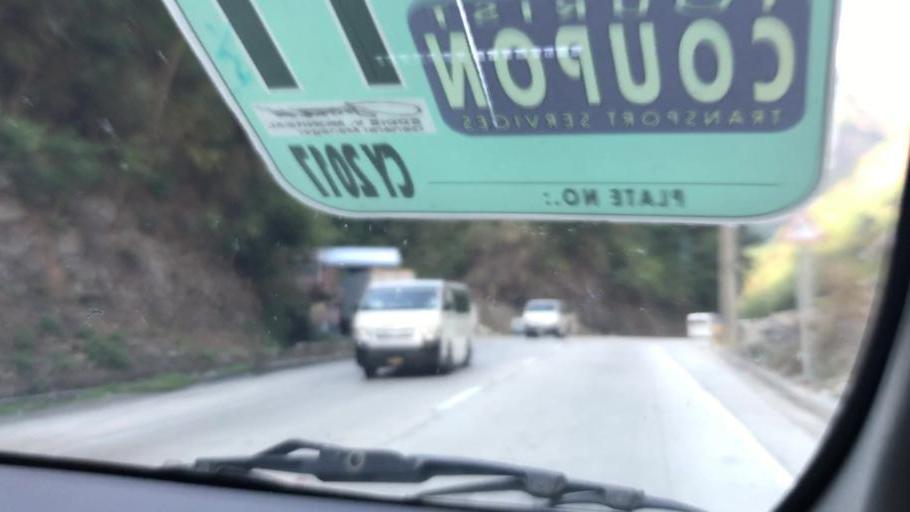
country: PH
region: Cordillera
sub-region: Province of Benguet
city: Tuba
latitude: 16.3236
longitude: 120.6147
